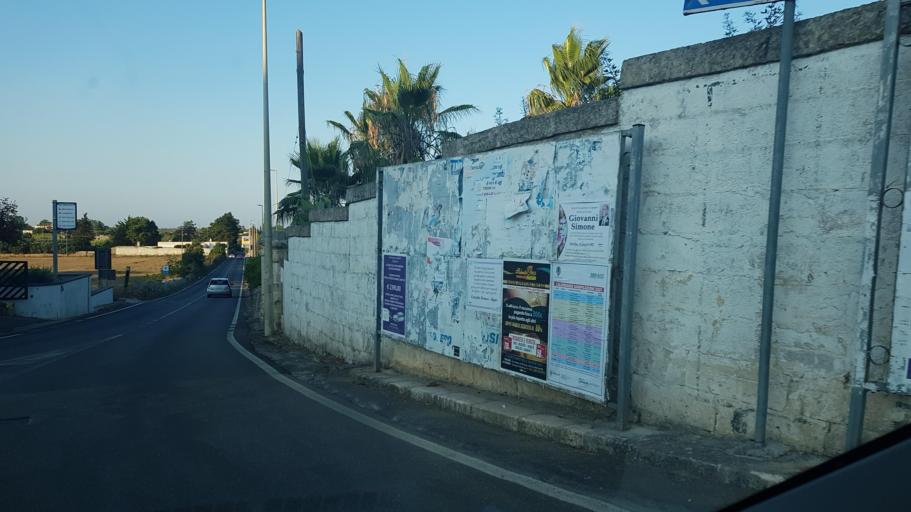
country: IT
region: Apulia
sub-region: Provincia di Lecce
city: Specchia
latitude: 39.9364
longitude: 18.3034
